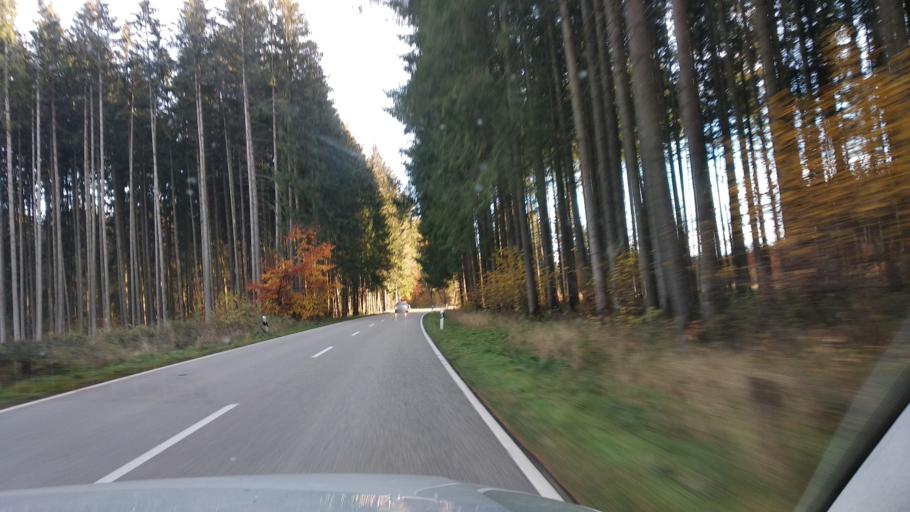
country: DE
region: Bavaria
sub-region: Upper Bavaria
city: Zorneding
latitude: 48.0689
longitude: 11.8394
